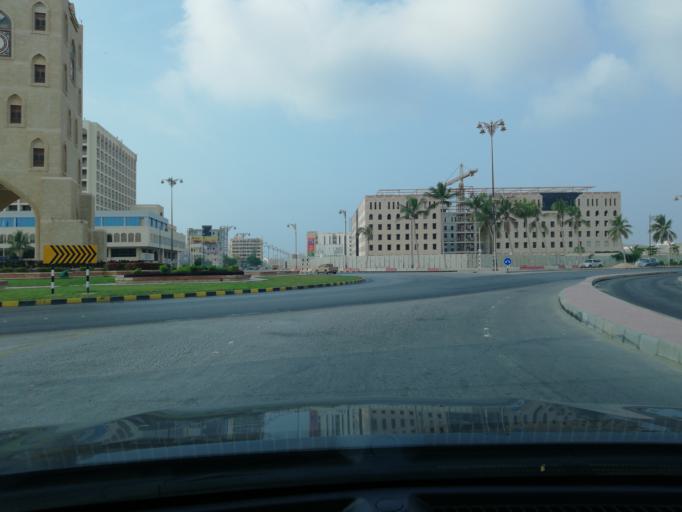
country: OM
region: Zufar
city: Salalah
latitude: 17.0256
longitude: 54.1116
